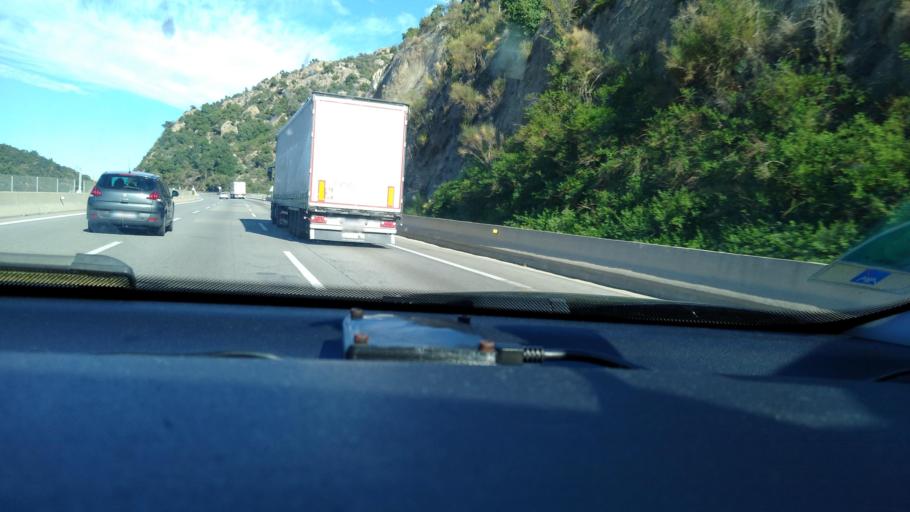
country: ES
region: Catalonia
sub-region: Provincia de Girona
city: la Jonquera
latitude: 42.4528
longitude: 2.8677
